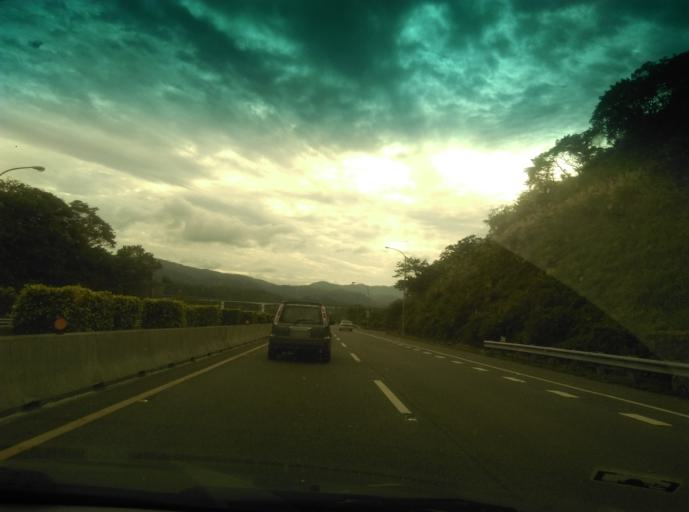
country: TW
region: Taiwan
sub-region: Keelung
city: Keelung
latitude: 25.1118
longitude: 121.7268
